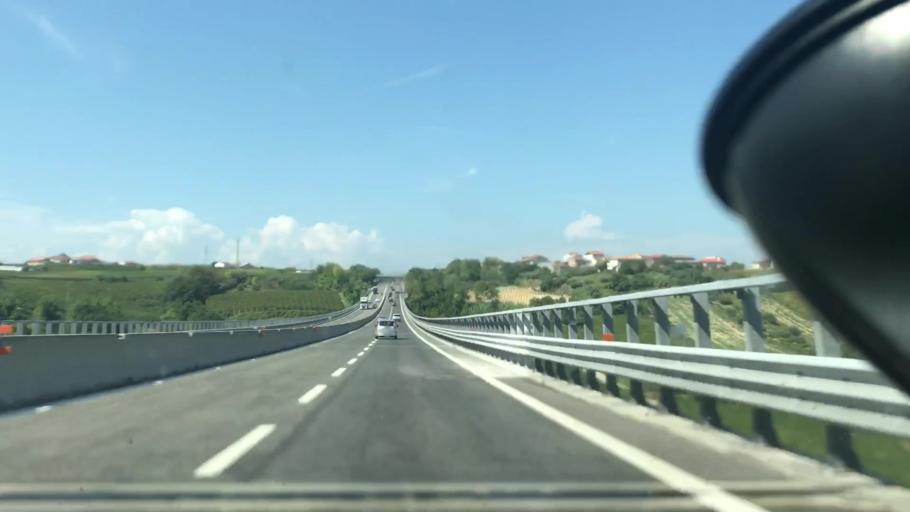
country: IT
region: Abruzzo
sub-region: Provincia di Chieti
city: Tollo
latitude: 42.3603
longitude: 14.3405
